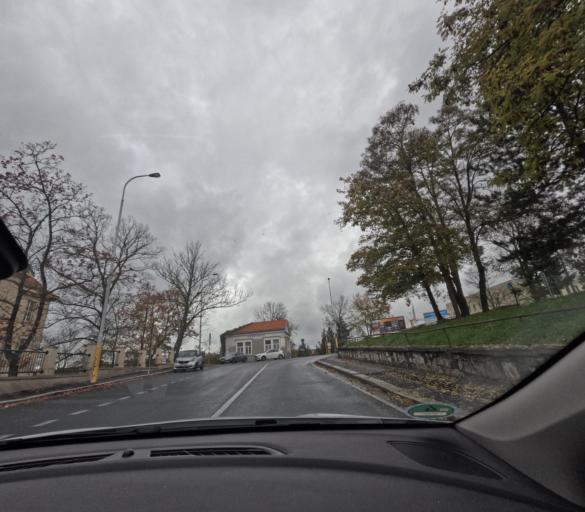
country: CZ
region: Karlovarsky
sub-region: Okres Karlovy Vary
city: Karlovy Vary
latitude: 50.2317
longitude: 12.8746
